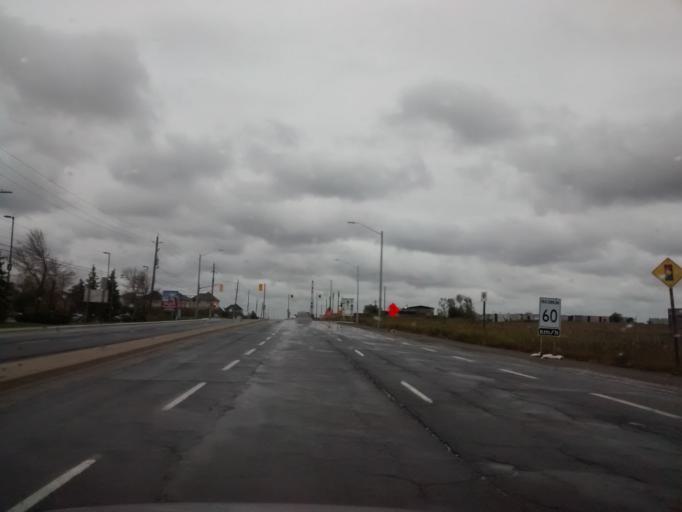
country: CA
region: Ontario
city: Hamilton
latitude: 43.1747
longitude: -79.7759
